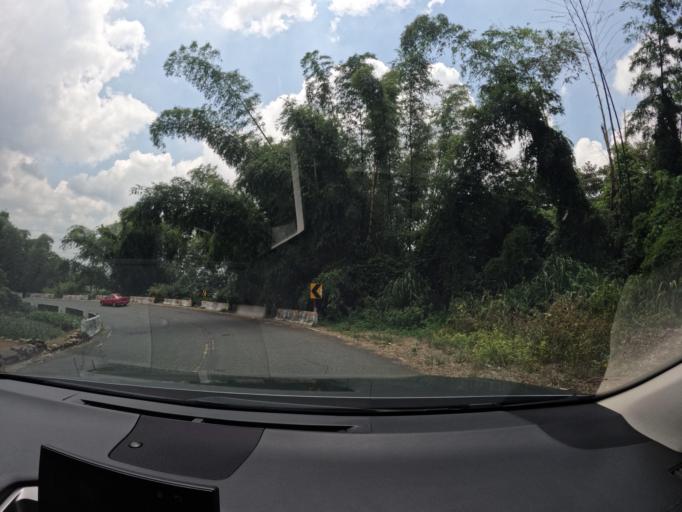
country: TW
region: Taiwan
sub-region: Nantou
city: Nantou
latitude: 23.8868
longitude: 120.6306
